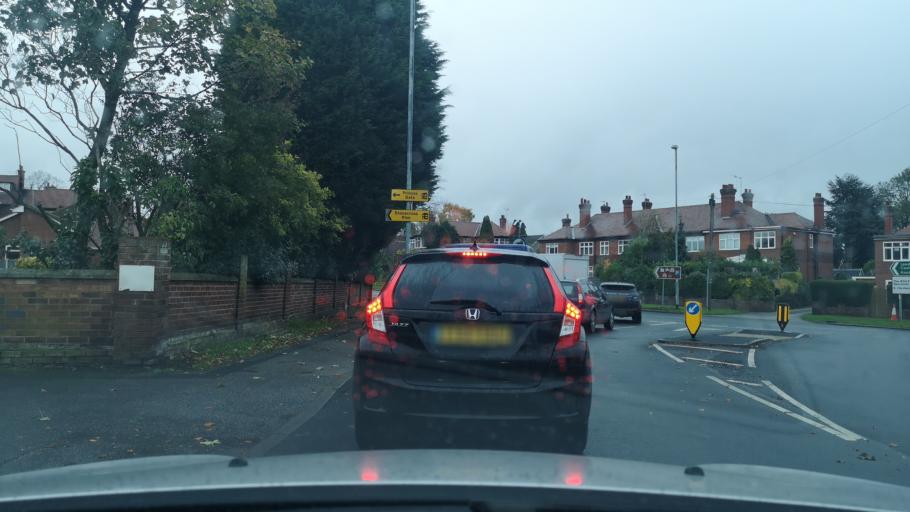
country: GB
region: England
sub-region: City and Borough of Wakefield
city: Pontefract
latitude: 53.6806
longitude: -1.3136
